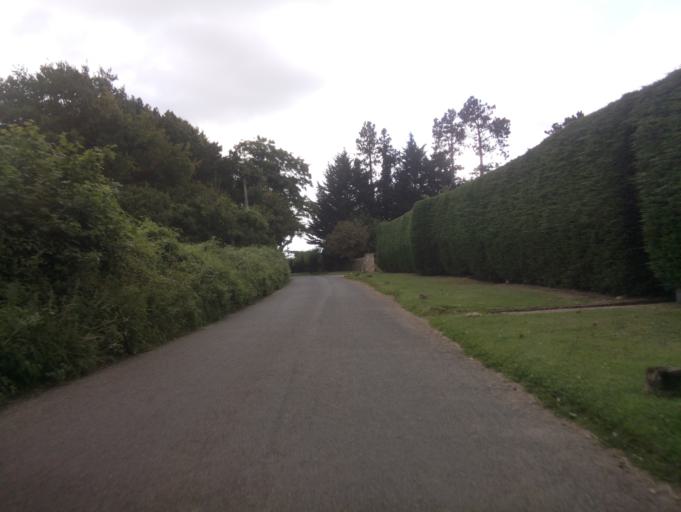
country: GB
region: England
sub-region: Gloucestershire
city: Chalford
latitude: 51.7648
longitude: -2.0891
